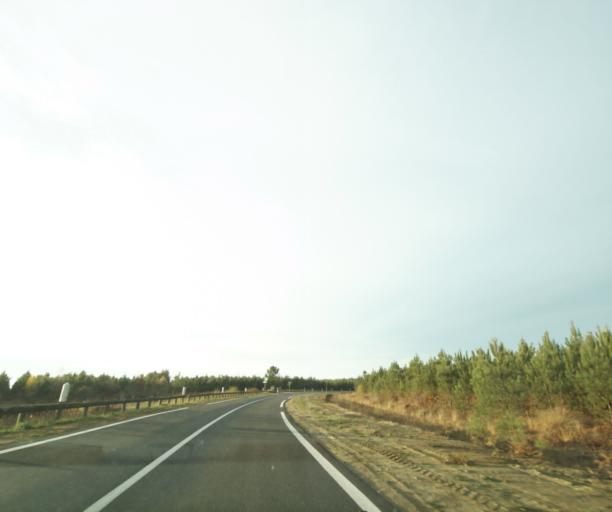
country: FR
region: Aquitaine
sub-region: Departement des Landes
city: Gabarret
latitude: 44.0854
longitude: -0.0917
